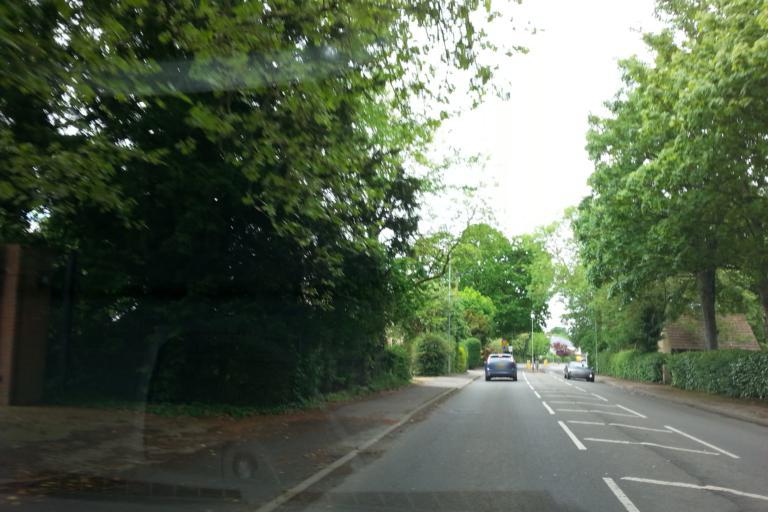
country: GB
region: England
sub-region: Cambridgeshire
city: Ramsey
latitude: 52.4453
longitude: -0.1121
